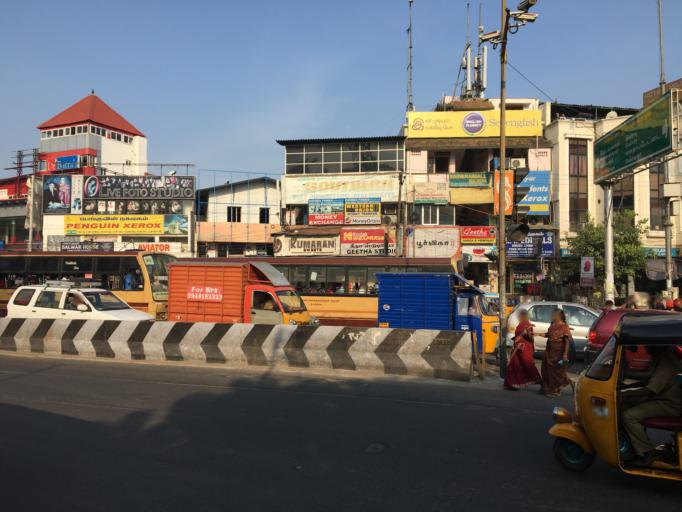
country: IN
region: Tamil Nadu
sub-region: Kancheepuram
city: Perungudi
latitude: 12.9756
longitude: 80.2208
